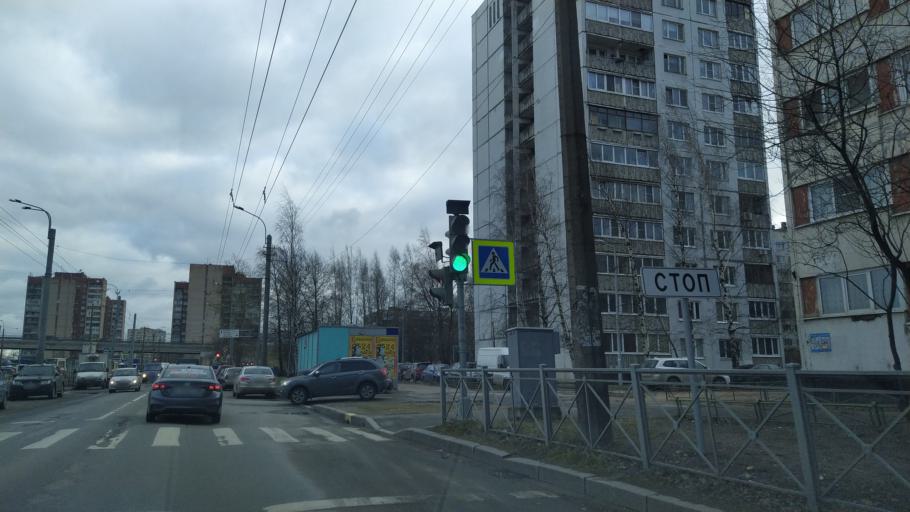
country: RU
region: Leningrad
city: Bugry
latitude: 60.0523
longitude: 30.3768
